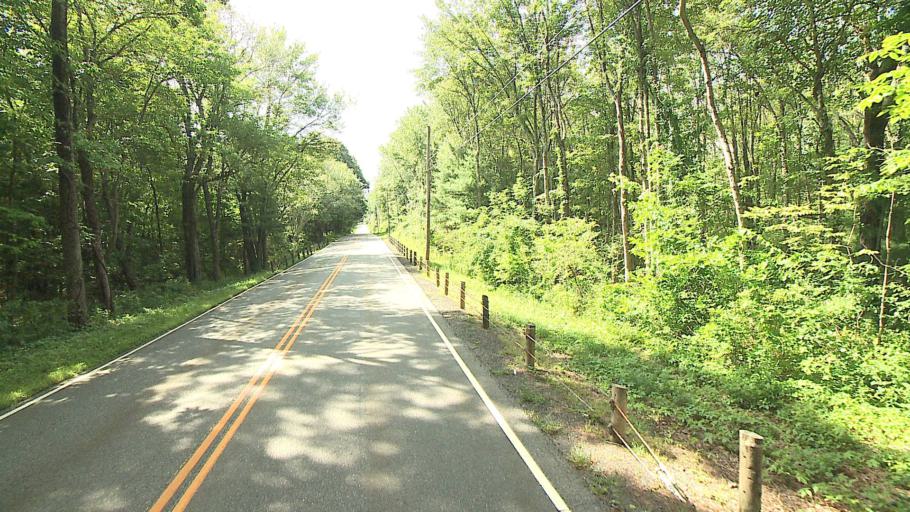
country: US
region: Connecticut
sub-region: Litchfield County
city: Litchfield
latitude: 41.6944
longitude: -73.1959
